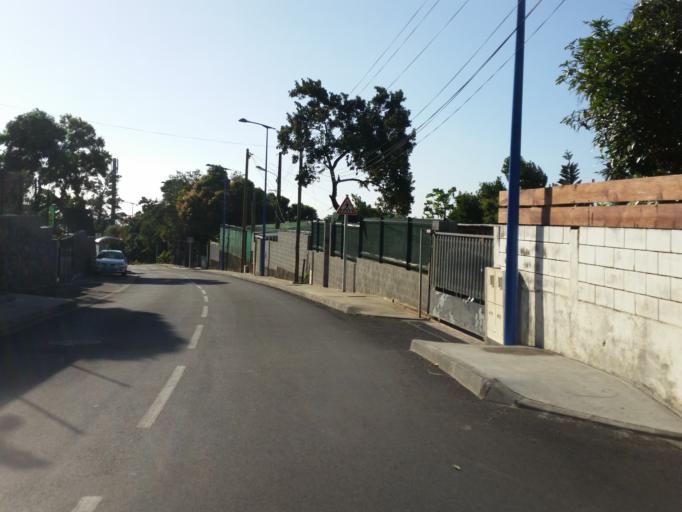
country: RE
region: Reunion
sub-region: Reunion
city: Sainte-Marie
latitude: -20.9242
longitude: 55.5186
